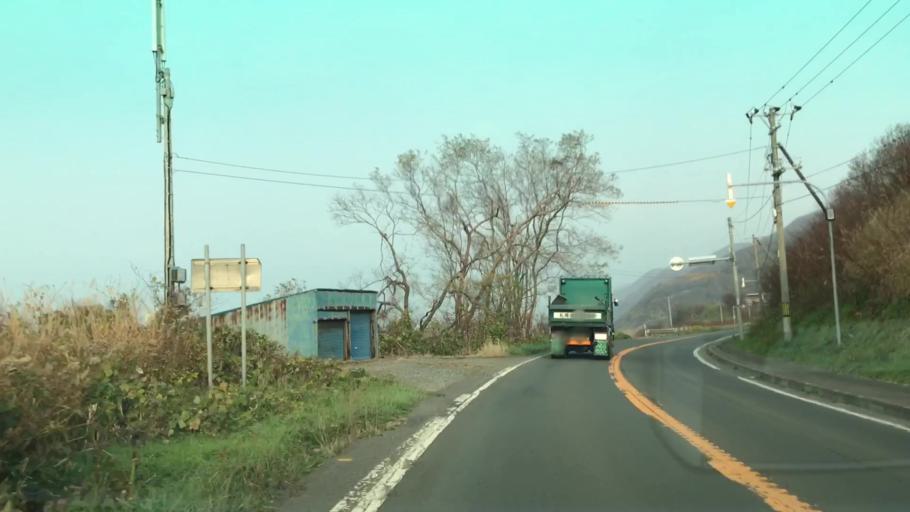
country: JP
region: Hokkaido
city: Ishikari
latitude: 43.4150
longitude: 141.4306
